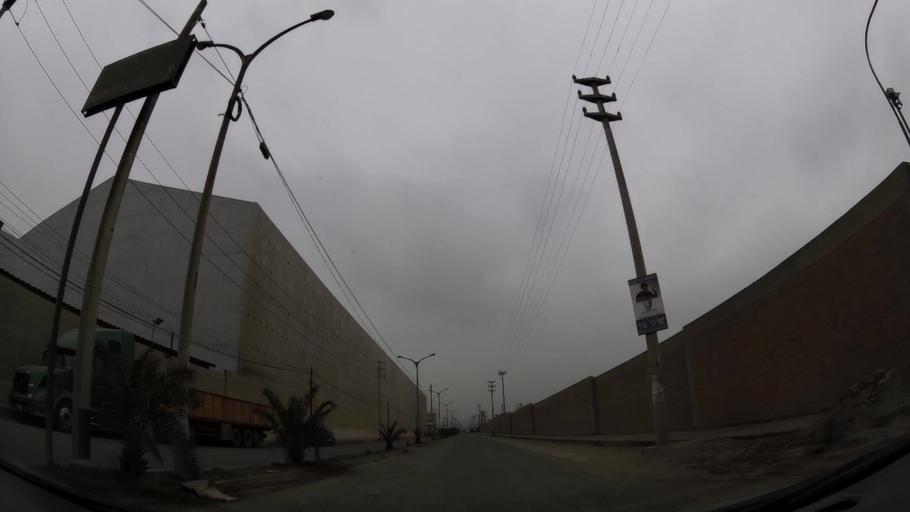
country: PE
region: Lima
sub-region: Lima
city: Punta Hermosa
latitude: -12.2967
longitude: -76.8396
